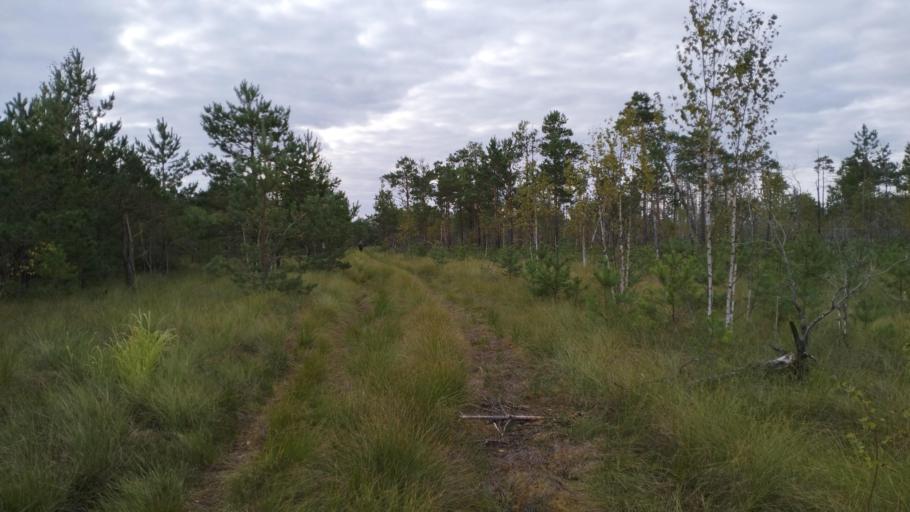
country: BY
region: Brest
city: Davyd-Haradok
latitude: 51.8956
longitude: 27.2126
